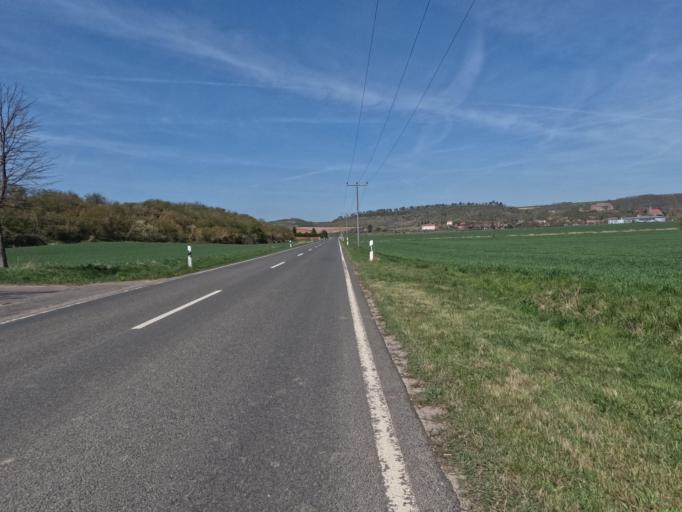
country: DE
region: Saxony-Anhalt
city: Beesenstedt
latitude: 51.6087
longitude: 11.7436
